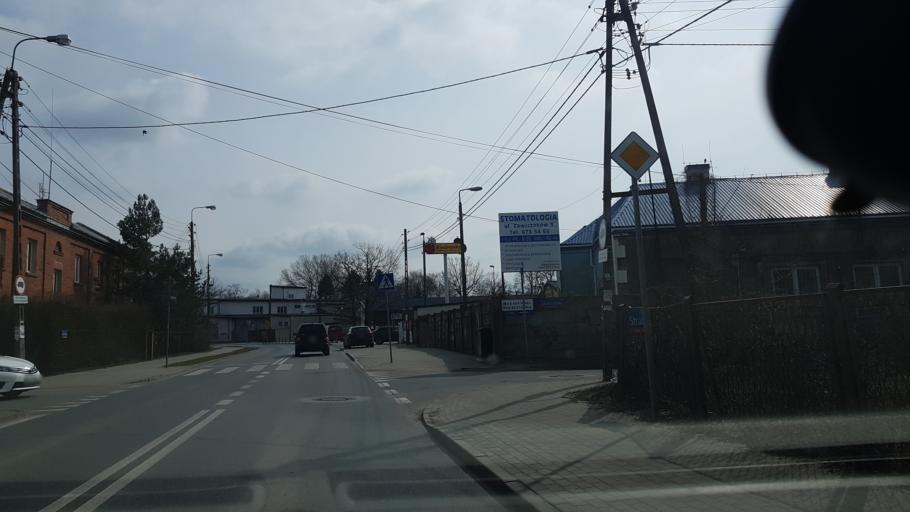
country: PL
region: Masovian Voivodeship
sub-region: Warszawa
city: Rembertow
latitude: 52.2596
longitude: 21.1550
